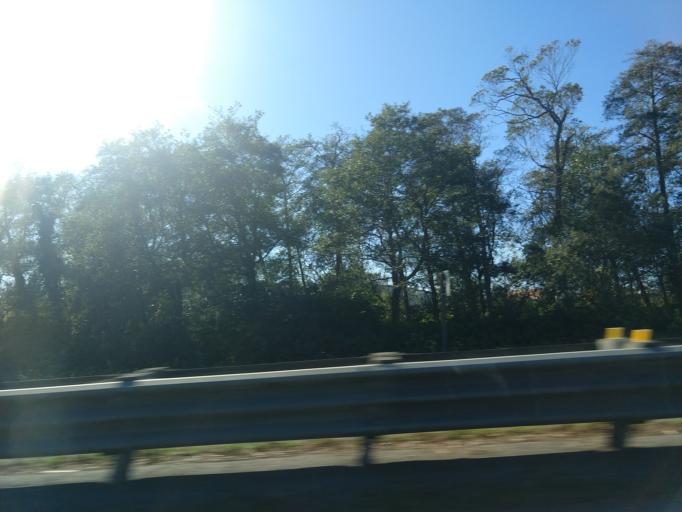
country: US
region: California
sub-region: Humboldt County
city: Fortuna
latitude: 40.5824
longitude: -124.1514
